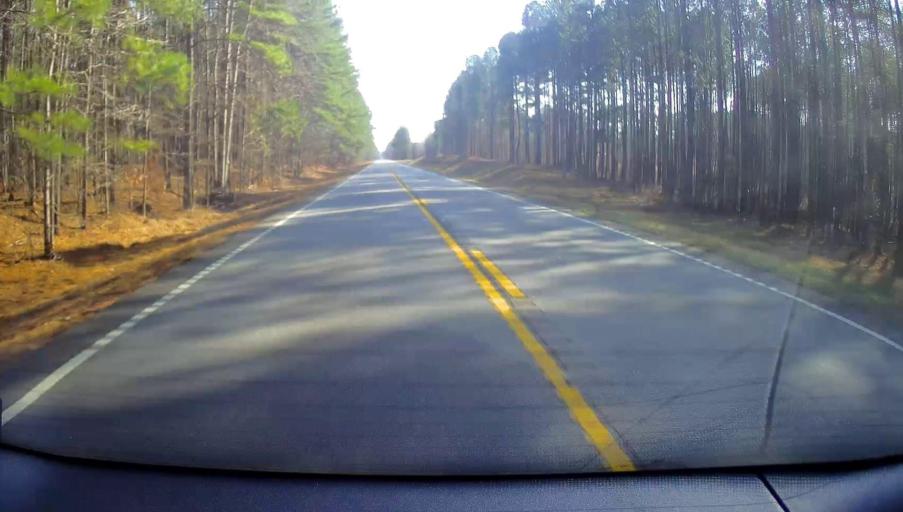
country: US
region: Georgia
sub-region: Butts County
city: Indian Springs
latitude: 33.1837
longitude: -83.8466
